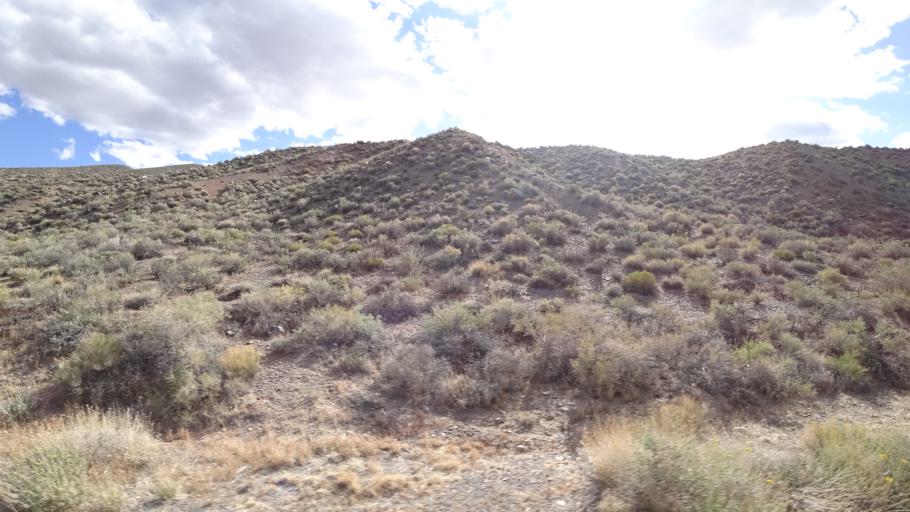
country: US
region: Nevada
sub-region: Nye County
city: Beatty
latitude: 36.4045
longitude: -117.1705
